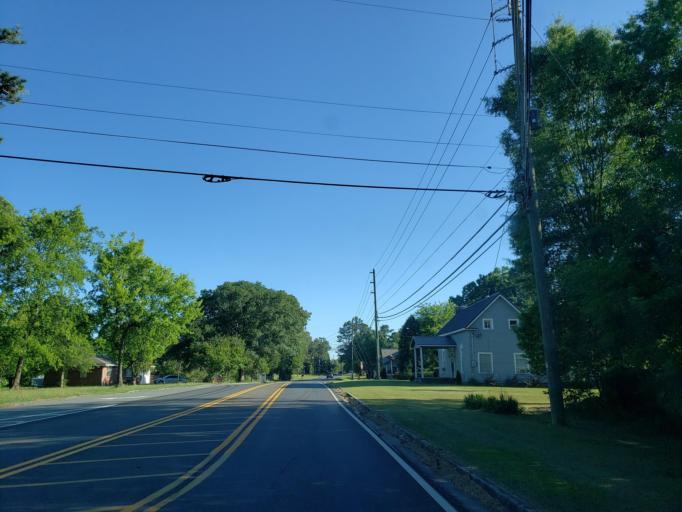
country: US
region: Georgia
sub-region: Floyd County
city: Rome
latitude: 34.3129
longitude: -85.1667
